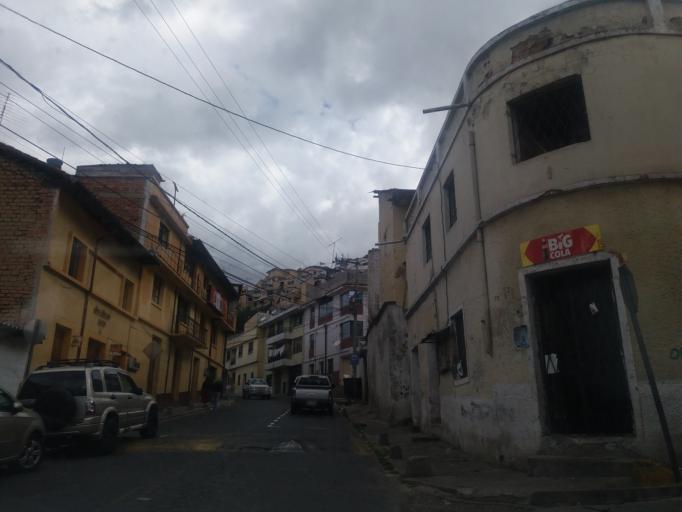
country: EC
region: Pichincha
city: Quito
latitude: -0.2200
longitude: -78.5239
